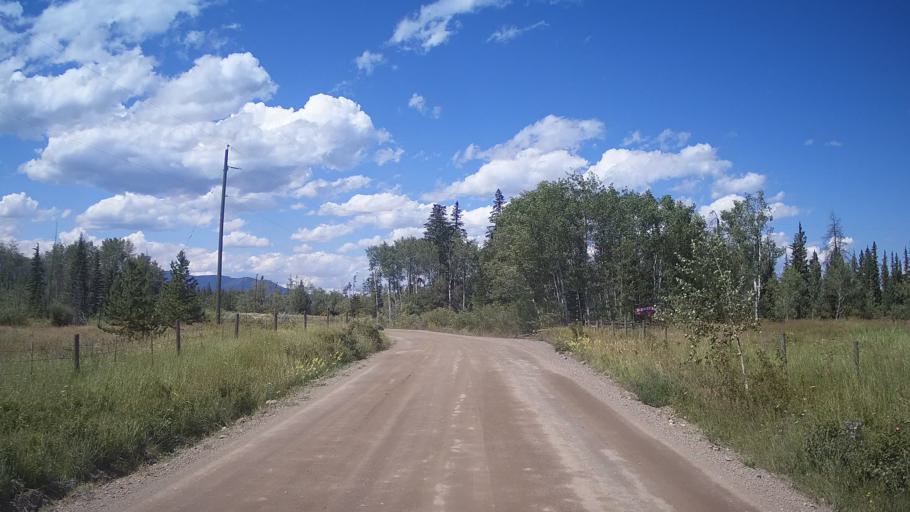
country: CA
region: British Columbia
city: Cache Creek
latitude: 51.2575
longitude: -121.6818
